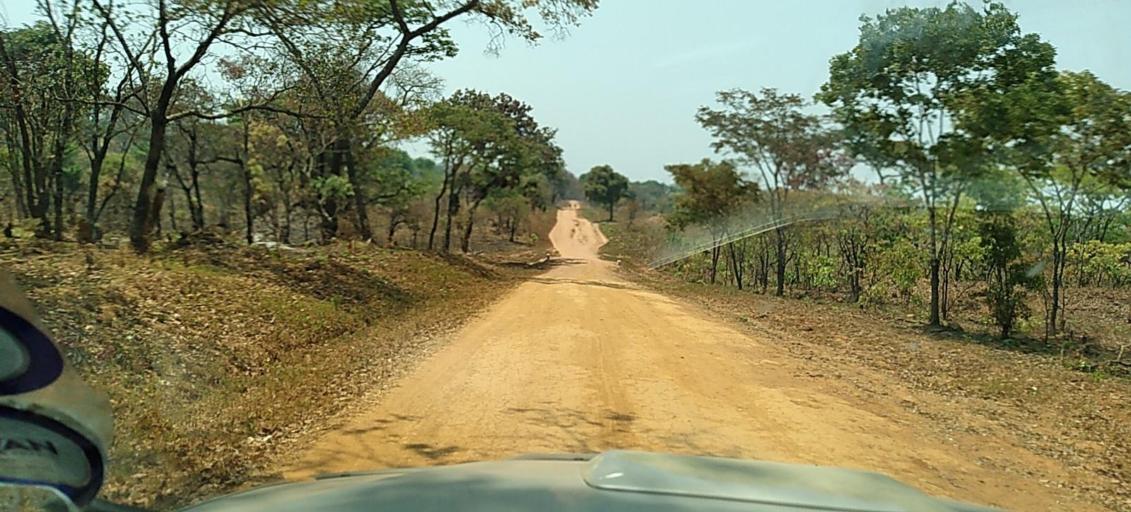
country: ZM
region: North-Western
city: Kasempa
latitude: -13.5449
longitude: 26.0411
